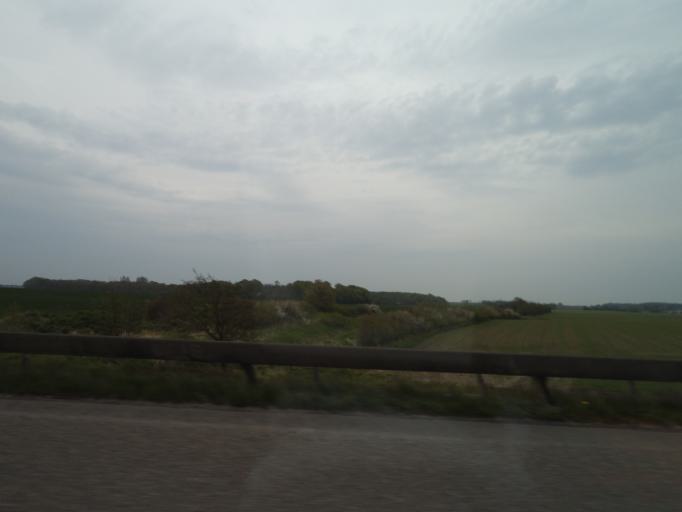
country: DK
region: Central Jutland
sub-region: Hedensted Kommune
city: Hedensted
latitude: 55.8280
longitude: 9.7042
